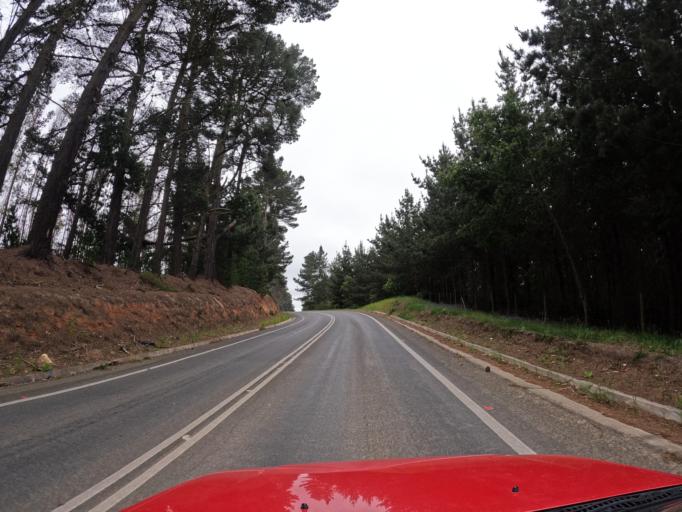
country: CL
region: O'Higgins
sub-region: Provincia de Colchagua
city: Santa Cruz
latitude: -34.5658
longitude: -72.0155
